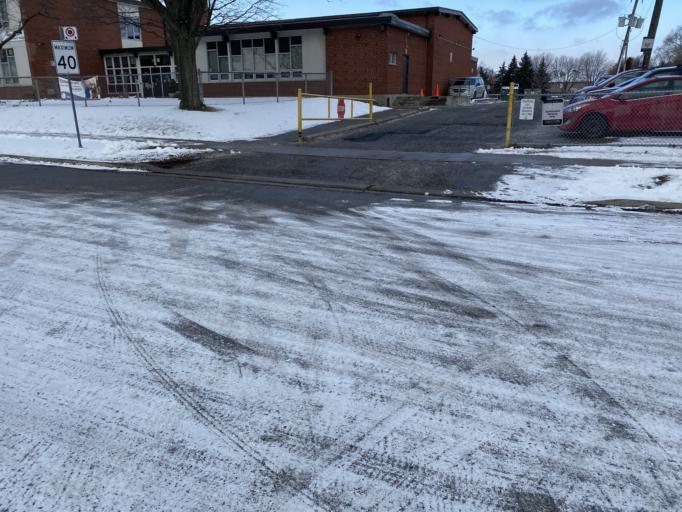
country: CA
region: Ontario
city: Scarborough
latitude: 43.7964
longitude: -79.2906
